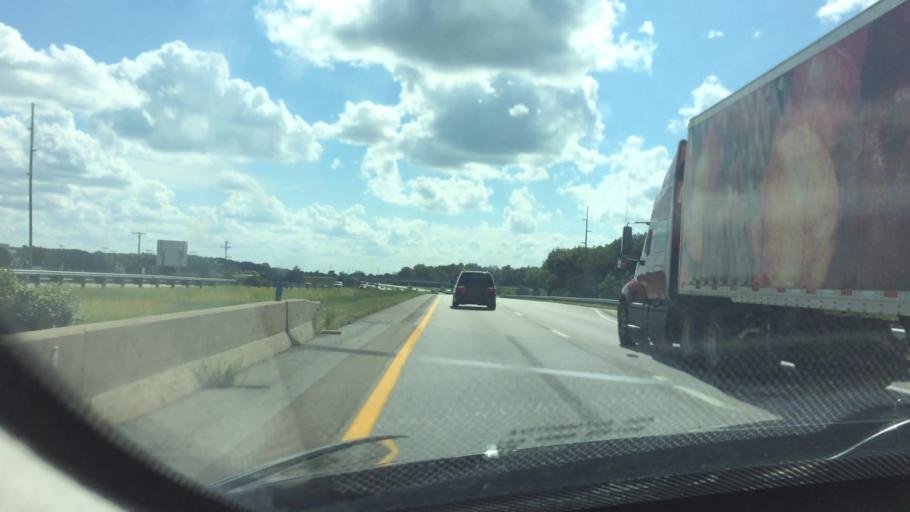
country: US
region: Ohio
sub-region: Shelby County
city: Sidney
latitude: 40.3175
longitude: -84.1703
